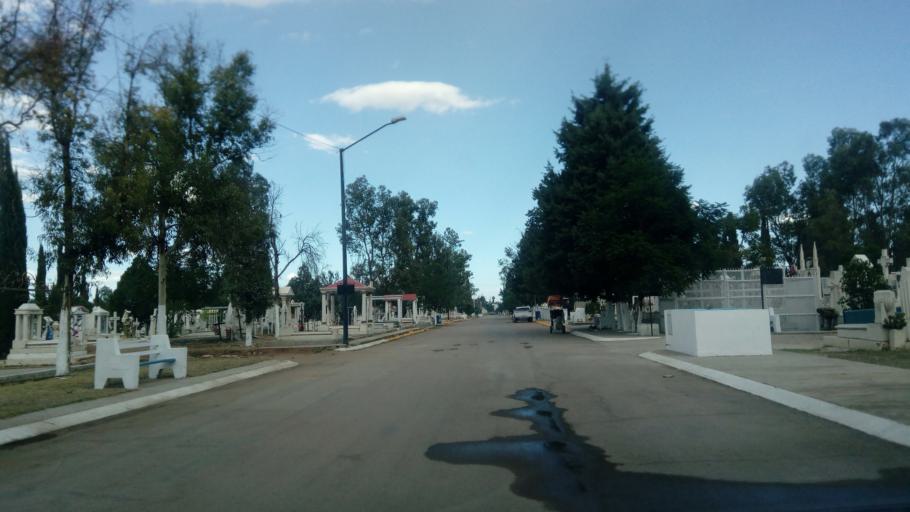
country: MX
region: Durango
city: Victoria de Durango
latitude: 24.0285
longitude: -104.6381
